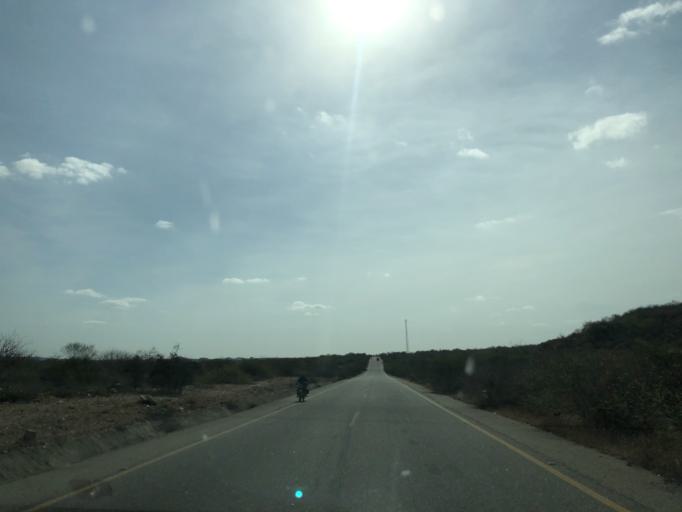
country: AO
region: Benguela
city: Benguela
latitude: -12.8931
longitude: 13.4871
